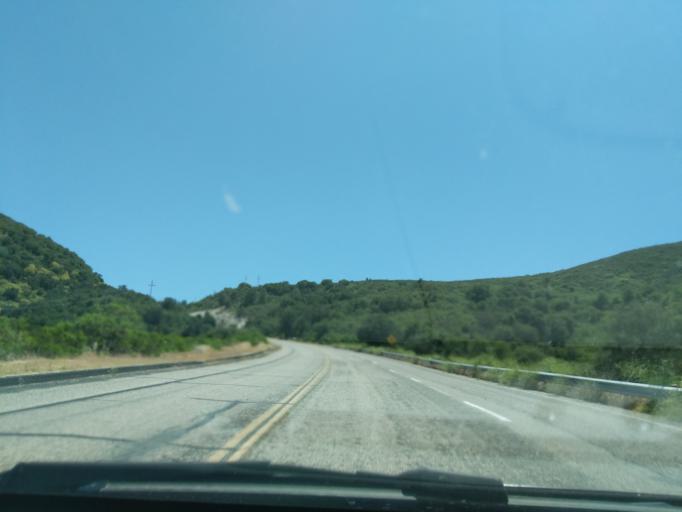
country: US
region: California
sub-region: Monterey County
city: King City
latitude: 36.0809
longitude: -121.1786
